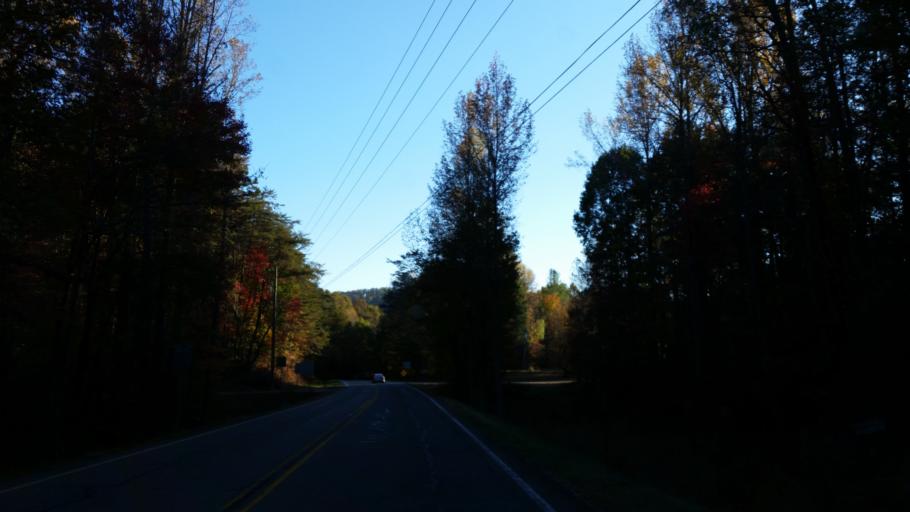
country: US
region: Georgia
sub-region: Pickens County
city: Jasper
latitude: 34.5794
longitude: -84.3025
